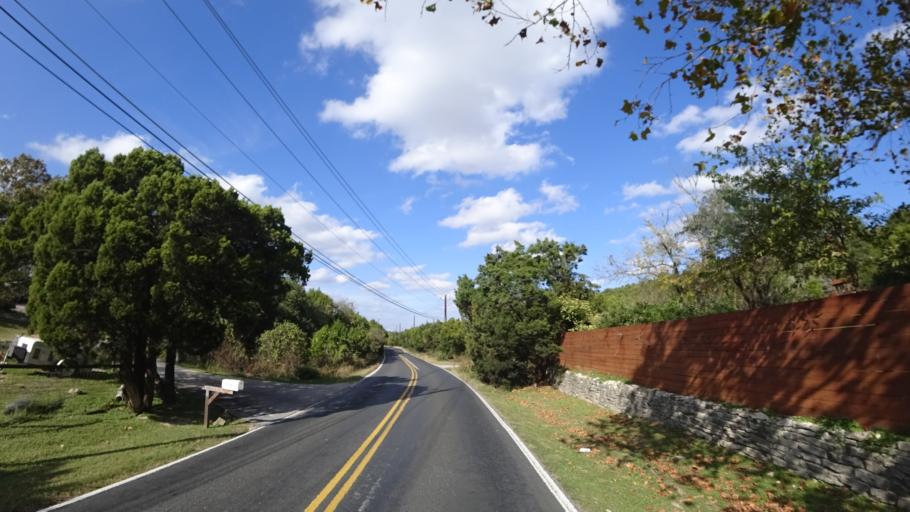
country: US
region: Texas
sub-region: Travis County
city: Barton Creek
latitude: 30.2590
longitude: -97.8883
